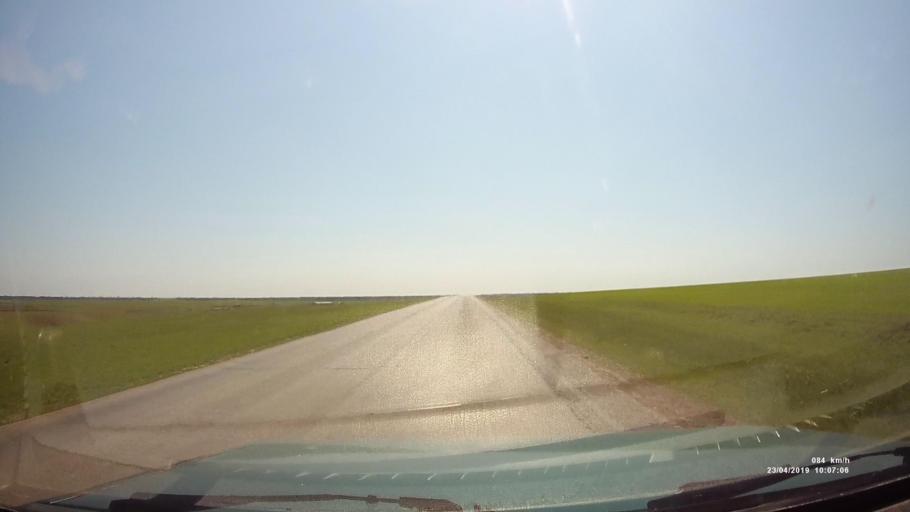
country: RU
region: Rostov
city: Sovetskoye
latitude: 46.7276
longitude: 42.2481
